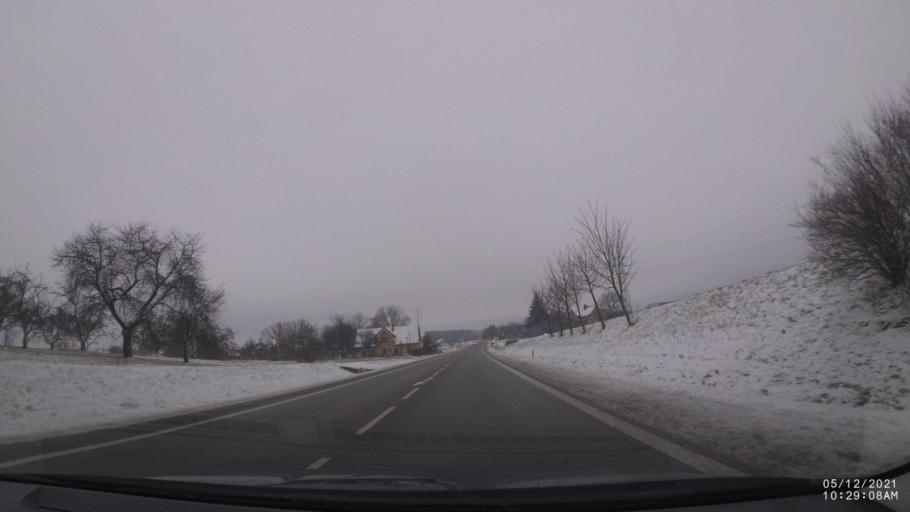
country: CZ
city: Vamberk
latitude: 50.1301
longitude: 16.2849
